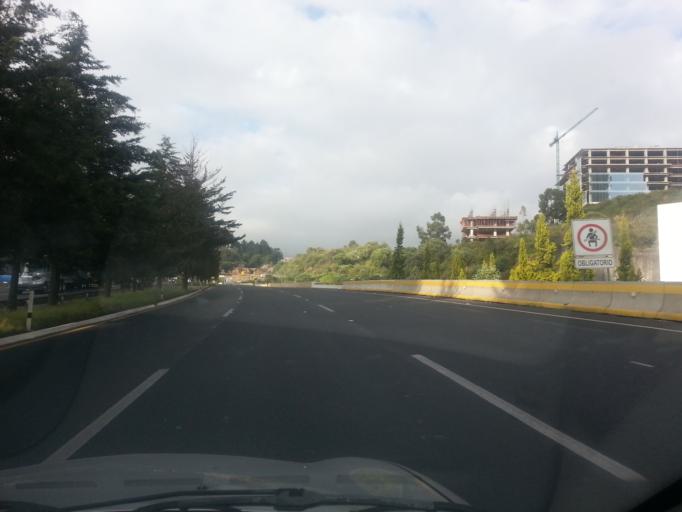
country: MX
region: Mexico City
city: Cuajimalpa
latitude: 19.3574
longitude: -99.2767
